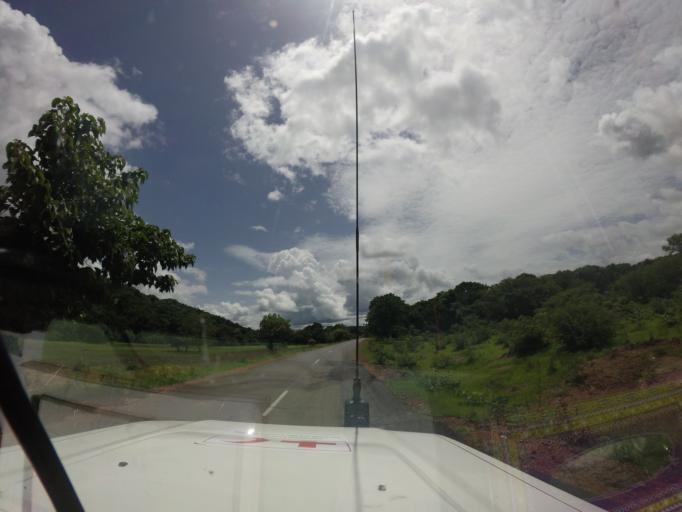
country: SL
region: Northern Province
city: Bindi
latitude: 10.1651
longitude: -11.2877
